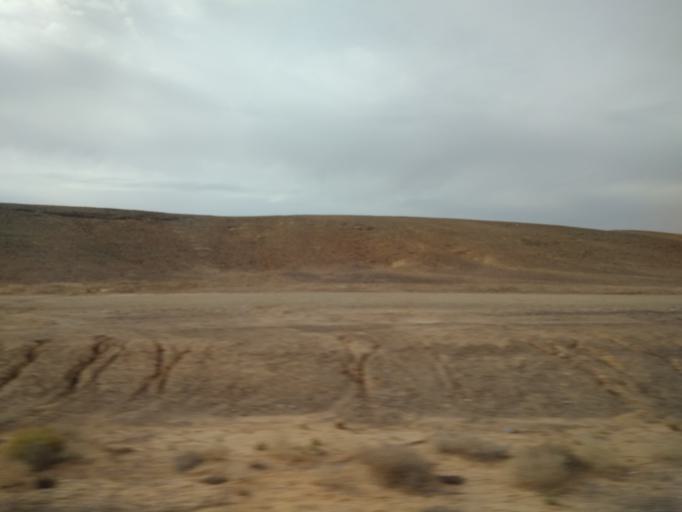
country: IL
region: Southern District
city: Eilat
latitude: 29.9129
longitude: 34.8775
